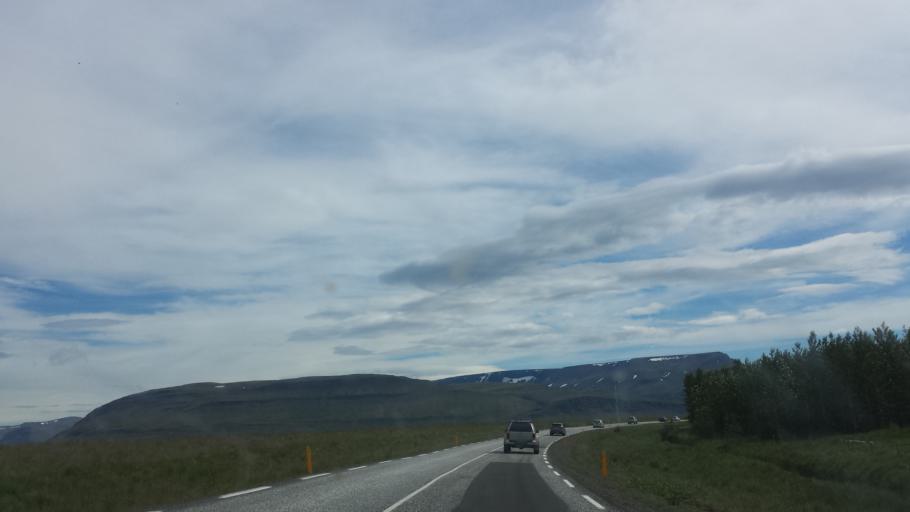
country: IS
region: West
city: Borgarnes
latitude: 64.3587
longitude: -21.8082
